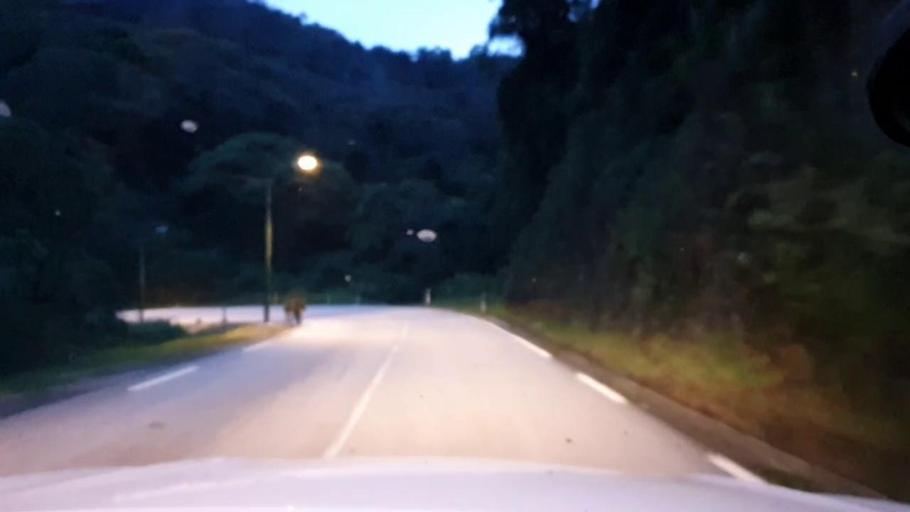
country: RW
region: Southern Province
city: Nzega
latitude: -2.5301
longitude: 29.3806
